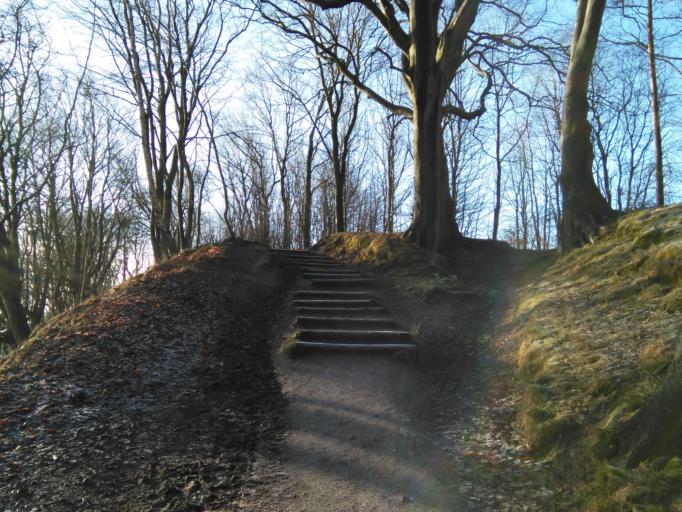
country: DK
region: Central Jutland
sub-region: Arhus Kommune
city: Arhus
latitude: 56.1151
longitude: 10.2288
